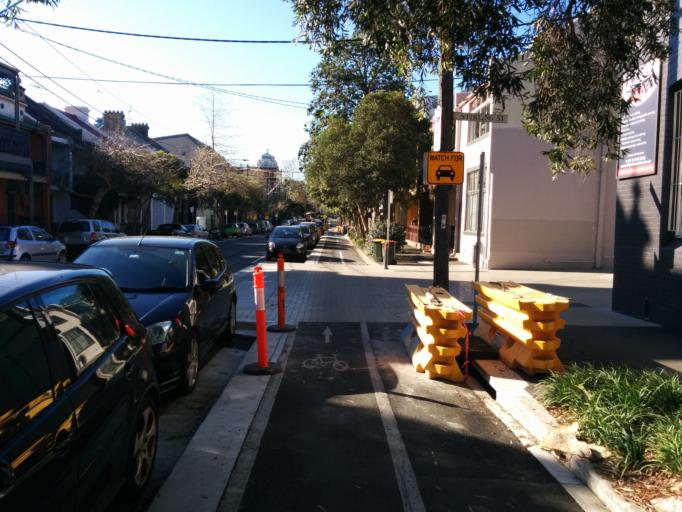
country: AU
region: New South Wales
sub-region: City of Sydney
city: Redfern
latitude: -33.8910
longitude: 151.2025
